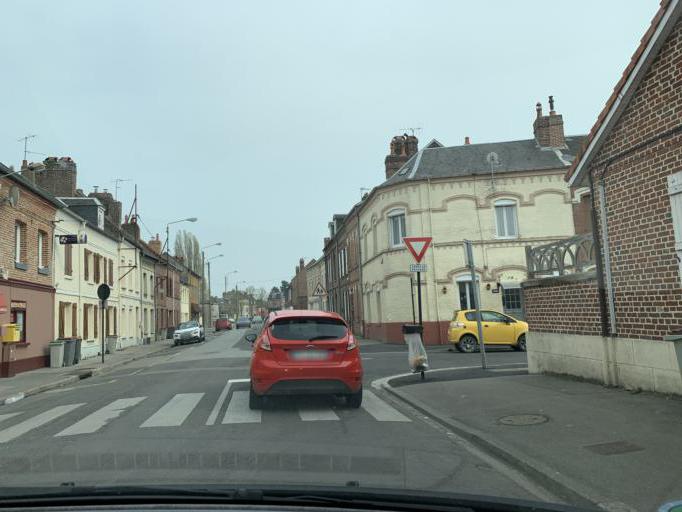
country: FR
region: Picardie
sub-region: Departement de la Somme
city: Abbeville
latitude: 50.1096
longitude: 1.8231
